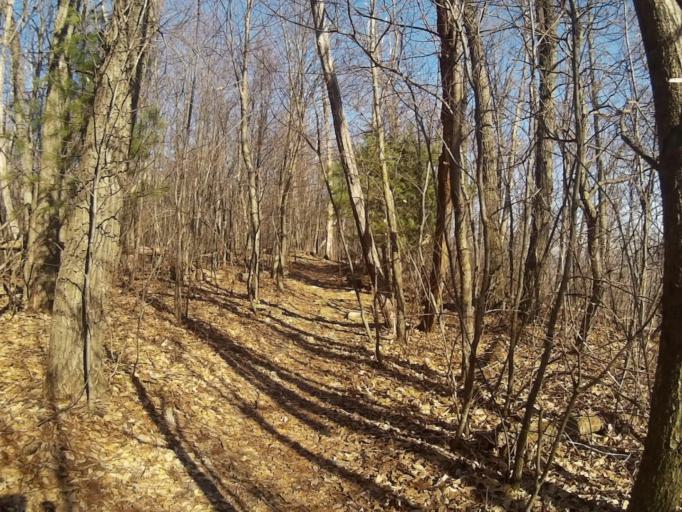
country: US
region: Pennsylvania
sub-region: Centre County
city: Boalsburg
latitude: 40.8088
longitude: -77.7837
